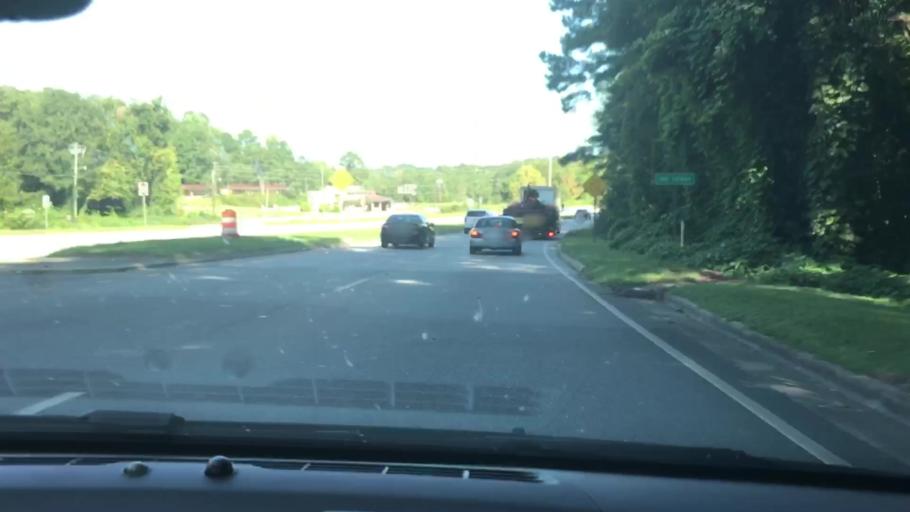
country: US
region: Alabama
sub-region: Barbour County
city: Eufaula
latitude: 31.9042
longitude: -85.1474
